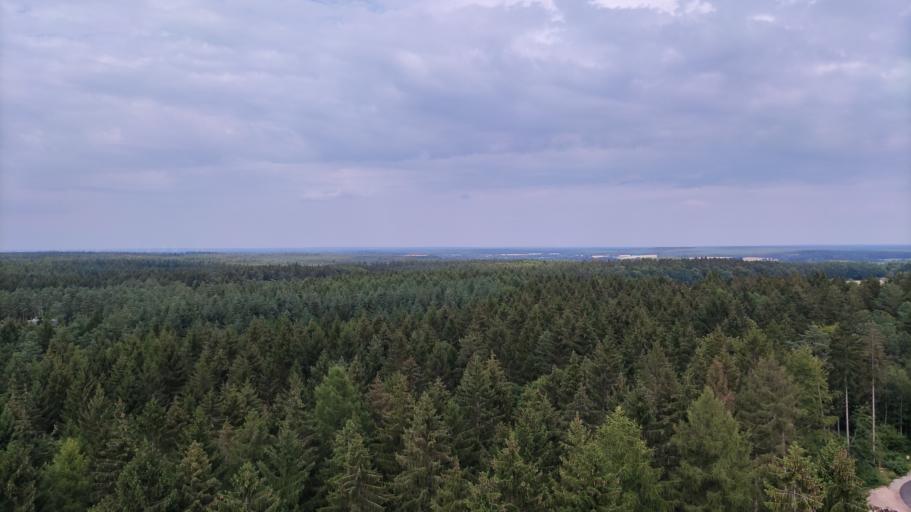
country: DE
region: Lower Saxony
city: Hanstedt
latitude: 53.2377
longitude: 10.0520
